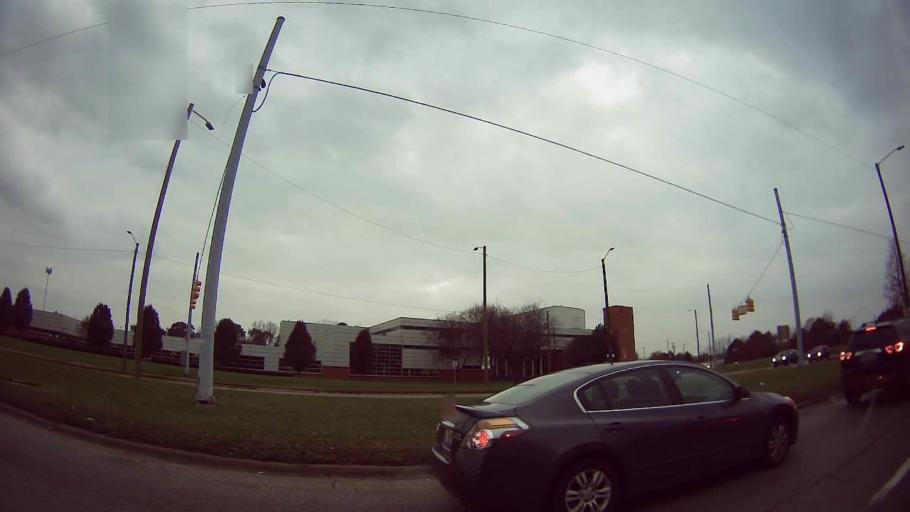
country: US
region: Michigan
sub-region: Wayne County
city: Grosse Pointe Park
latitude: 42.3931
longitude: -82.9832
